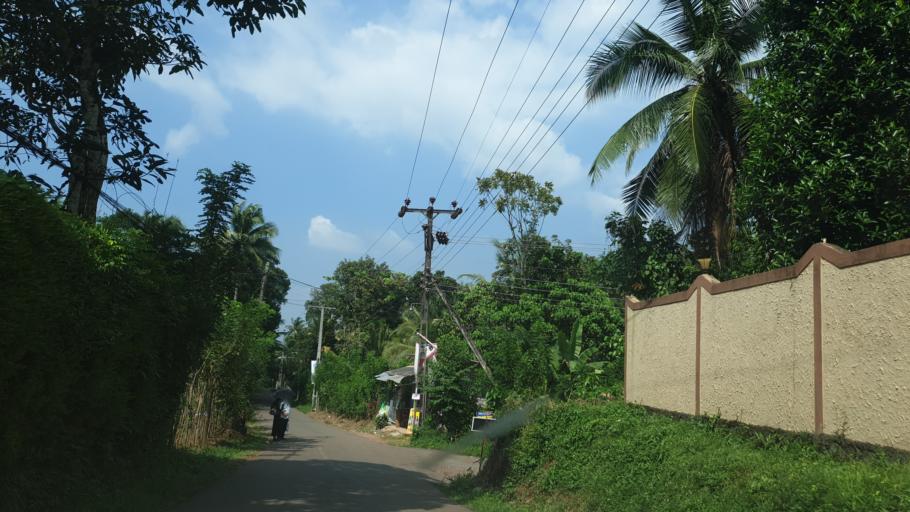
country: LK
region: Western
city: Panadura
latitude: 6.7371
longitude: 79.9518
